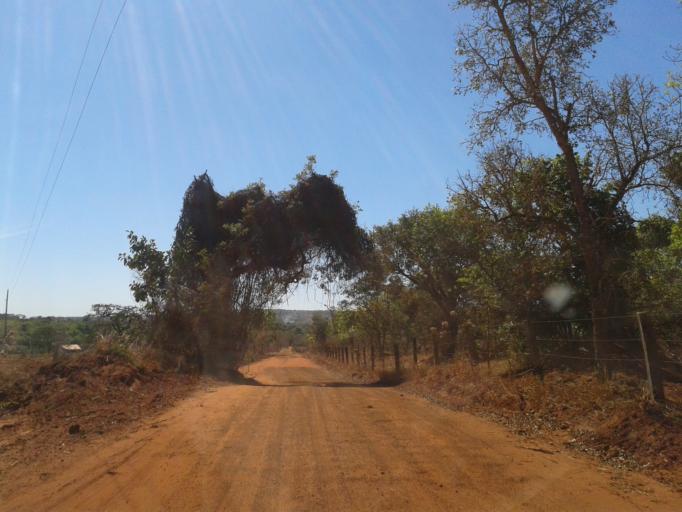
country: BR
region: Minas Gerais
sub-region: Ituiutaba
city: Ituiutaba
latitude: -19.0716
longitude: -49.3183
